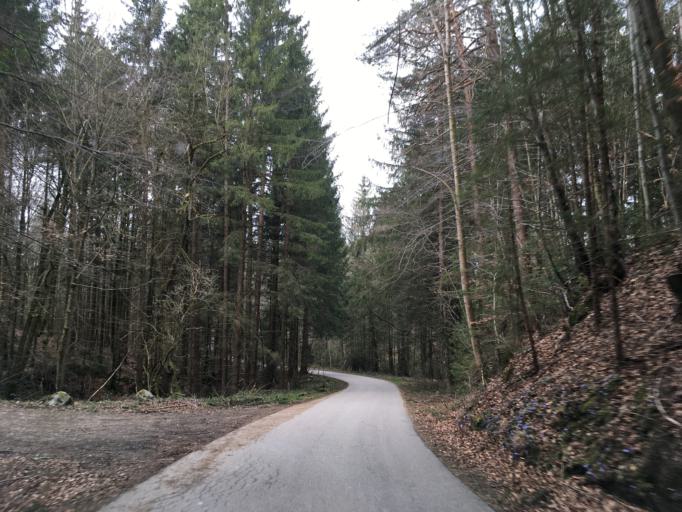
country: DE
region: Bavaria
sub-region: Upper Bavaria
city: Amerang
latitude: 47.9860
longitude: 12.3224
